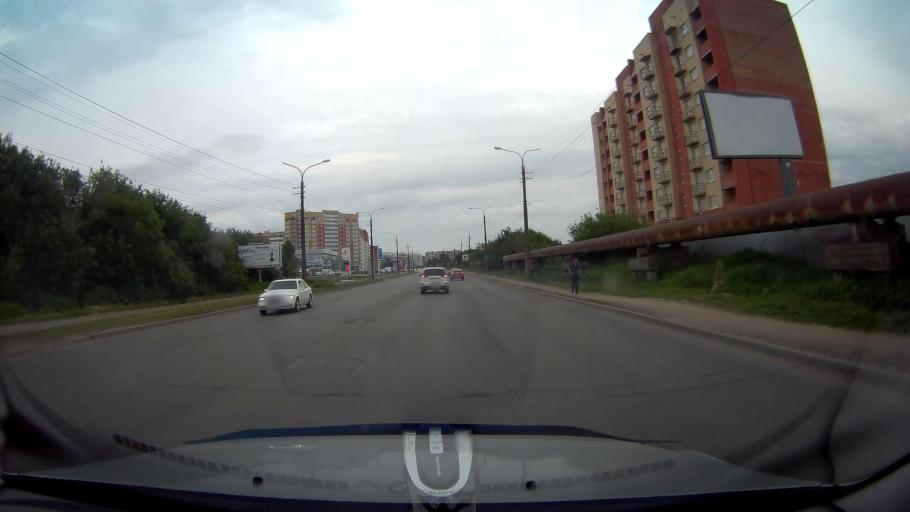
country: RU
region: Arkhangelskaya
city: Arkhangel'sk
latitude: 64.5318
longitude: 40.6028
